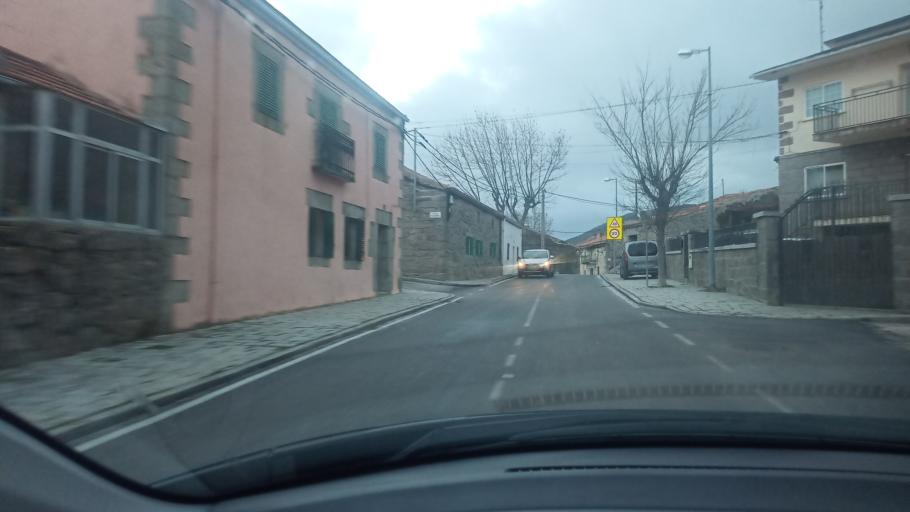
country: ES
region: Madrid
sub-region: Provincia de Madrid
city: Zarzalejo
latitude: 40.5479
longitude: -4.1802
